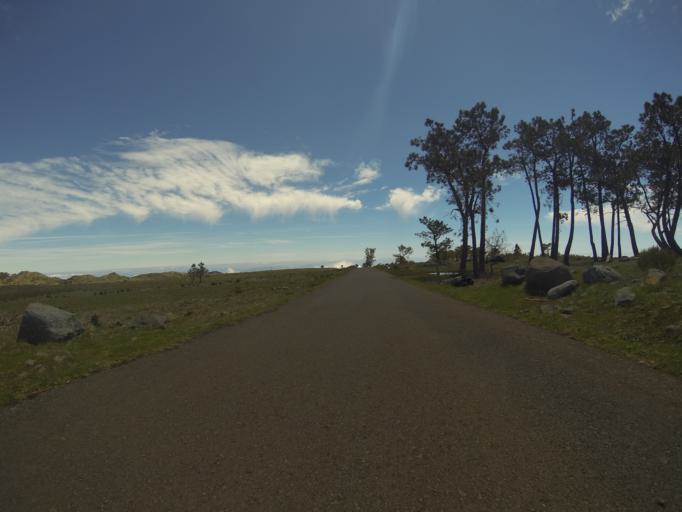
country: PT
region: Madeira
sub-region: Funchal
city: Nossa Senhora do Monte
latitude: 32.7137
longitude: -16.9092
